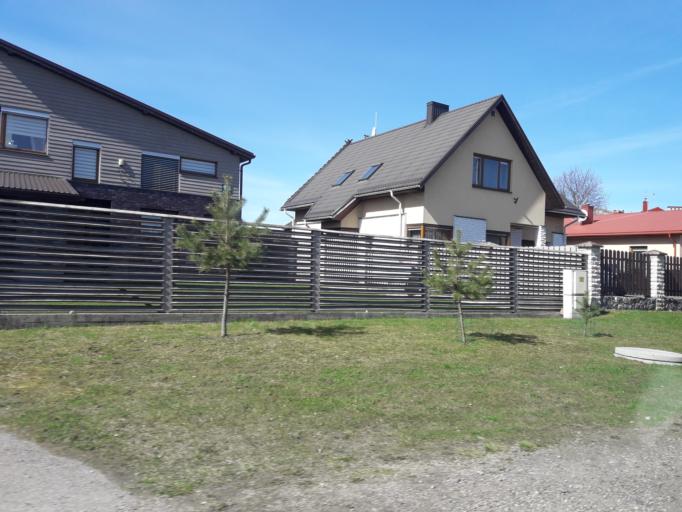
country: LT
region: Siauliu apskritis
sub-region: Siauliai
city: Siauliai
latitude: 55.9421
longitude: 23.3182
